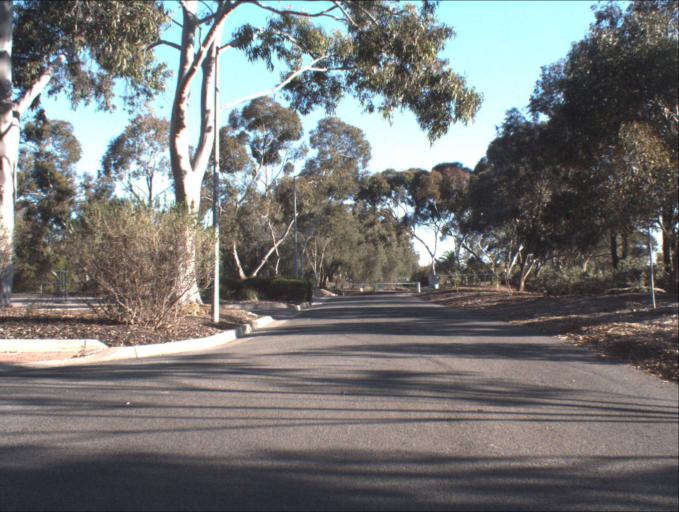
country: AU
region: South Australia
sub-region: Salisbury
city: Ingle Farm
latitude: -34.8400
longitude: 138.6256
